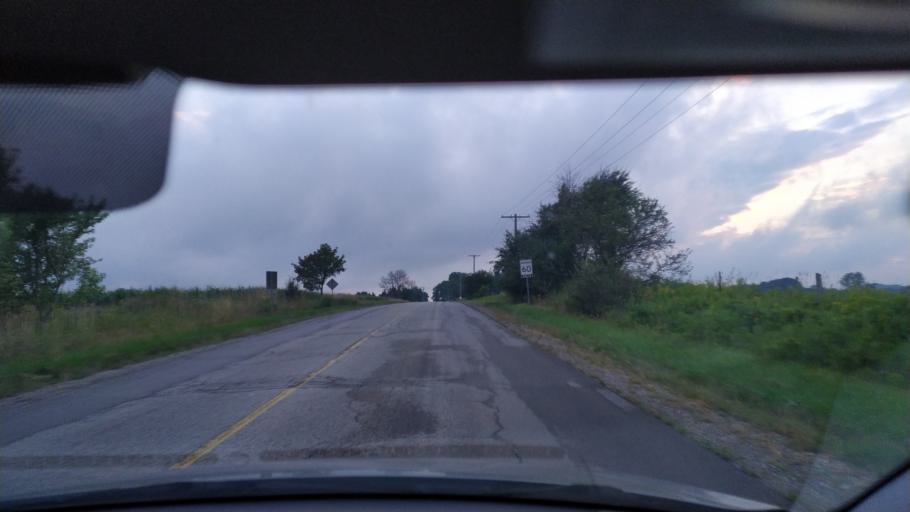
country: CA
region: Ontario
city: Kitchener
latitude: 43.3574
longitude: -80.6512
